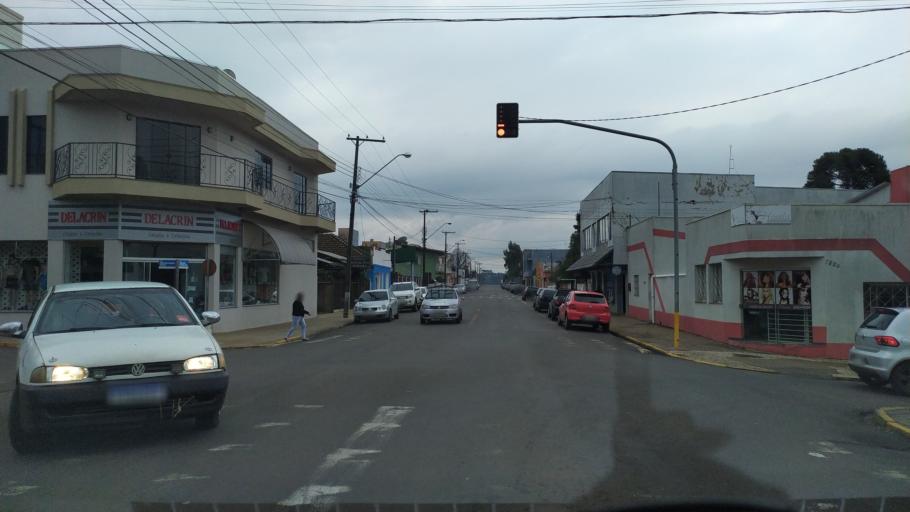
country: BR
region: Parana
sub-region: Palmas
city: Palmas
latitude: -26.4822
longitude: -51.9942
